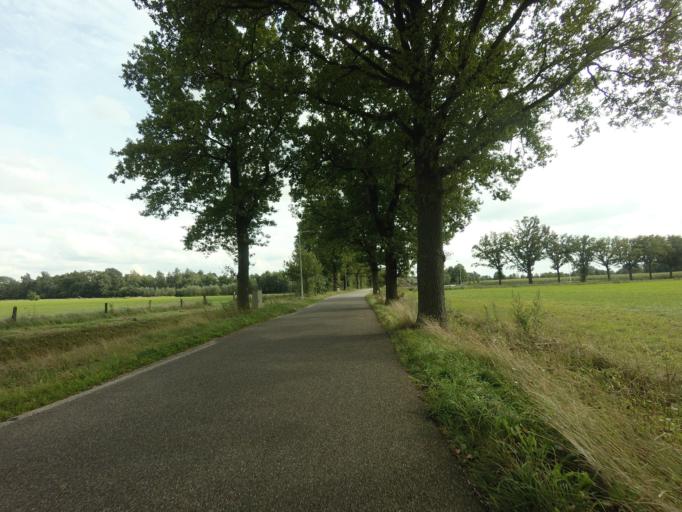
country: NL
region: Overijssel
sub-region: Gemeente Enschede
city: Enschede
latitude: 52.2025
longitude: 6.9568
